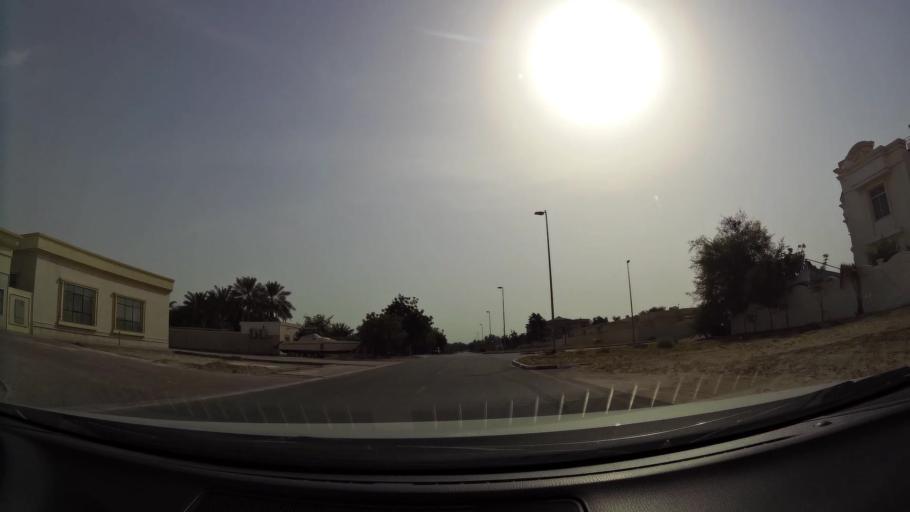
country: AE
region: Ash Shariqah
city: Sharjah
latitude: 25.2532
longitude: 55.4286
